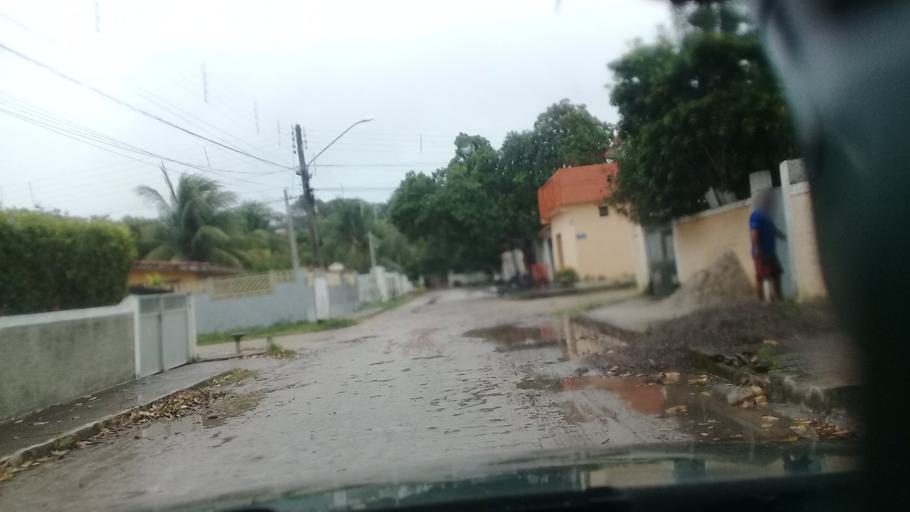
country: BR
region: Pernambuco
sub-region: Itamaraca
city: Itamaraca
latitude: -7.7361
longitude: -34.8277
